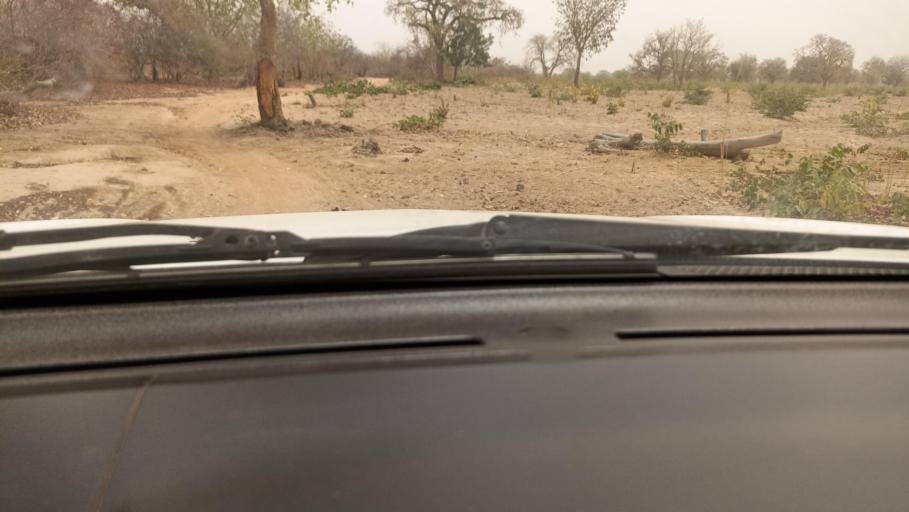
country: BF
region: Boucle du Mouhoun
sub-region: Province du Nayala
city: Toma
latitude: 12.8722
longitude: -2.7580
